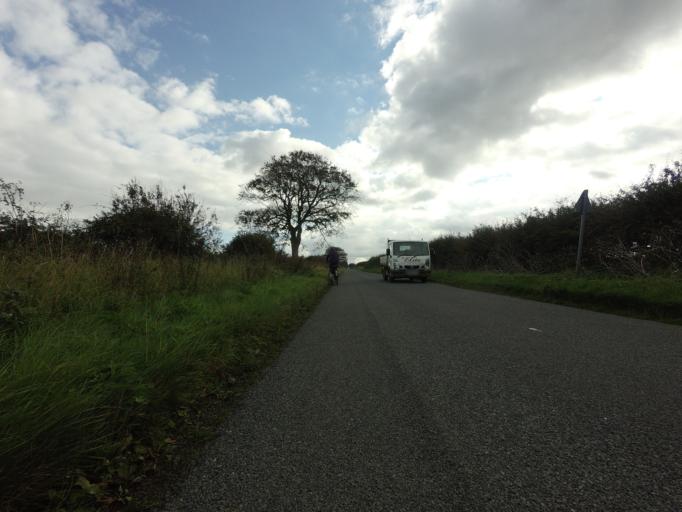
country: GB
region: England
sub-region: Norfolk
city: Hunstanton
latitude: 52.9253
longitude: 0.5398
